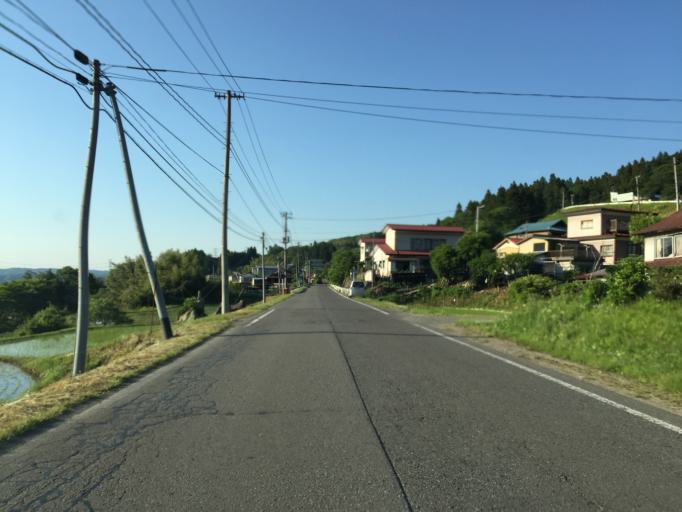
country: JP
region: Ibaraki
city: Daigo
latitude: 36.9312
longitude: 140.4457
